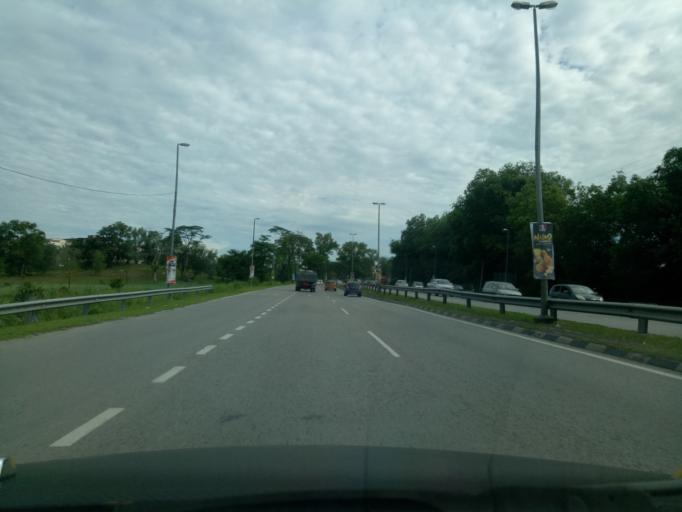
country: MY
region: Sarawak
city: Kuching
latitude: 1.4494
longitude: 110.3271
